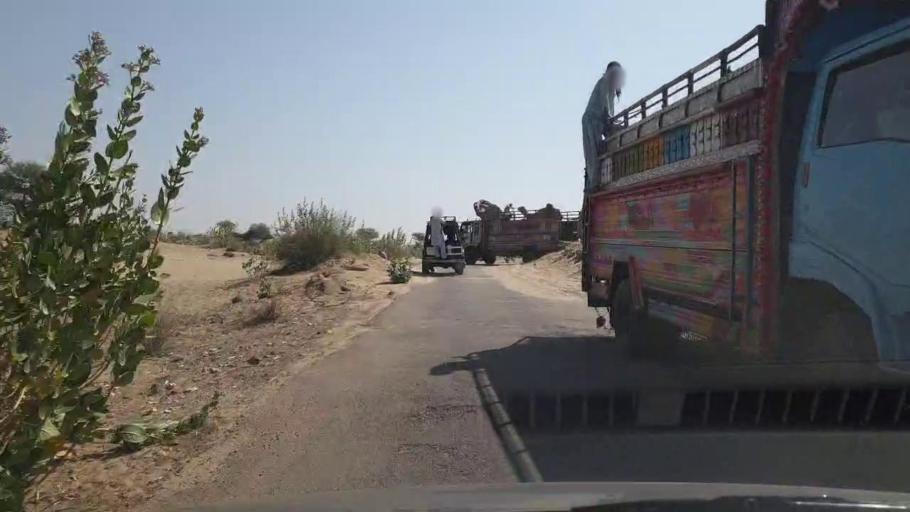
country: PK
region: Sindh
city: Chor
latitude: 25.5998
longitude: 70.0044
